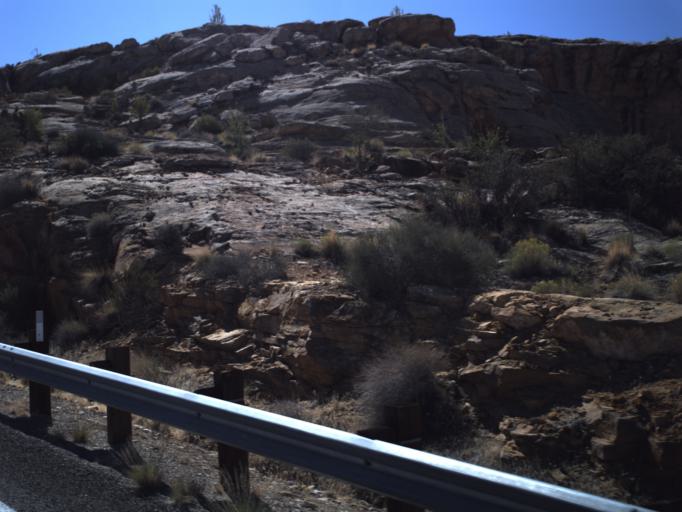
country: US
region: Utah
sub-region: San Juan County
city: Blanding
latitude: 37.8893
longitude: -110.3691
